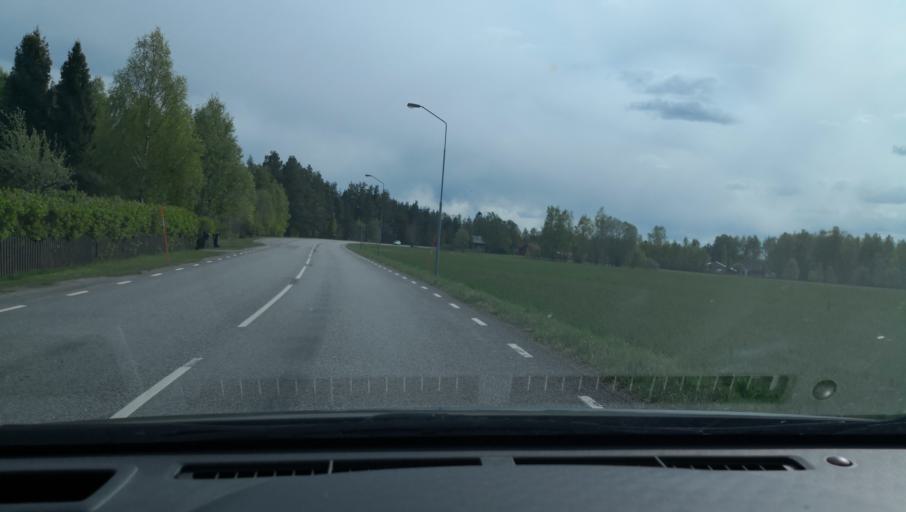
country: SE
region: OErebro
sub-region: Kumla Kommun
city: Kumla
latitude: 59.0852
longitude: 15.1577
